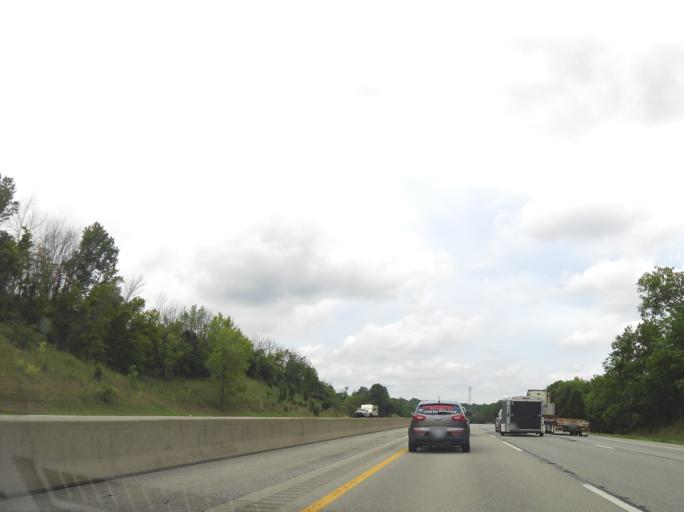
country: US
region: Kentucky
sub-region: Scott County
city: Georgetown
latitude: 38.3537
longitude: -84.5674
